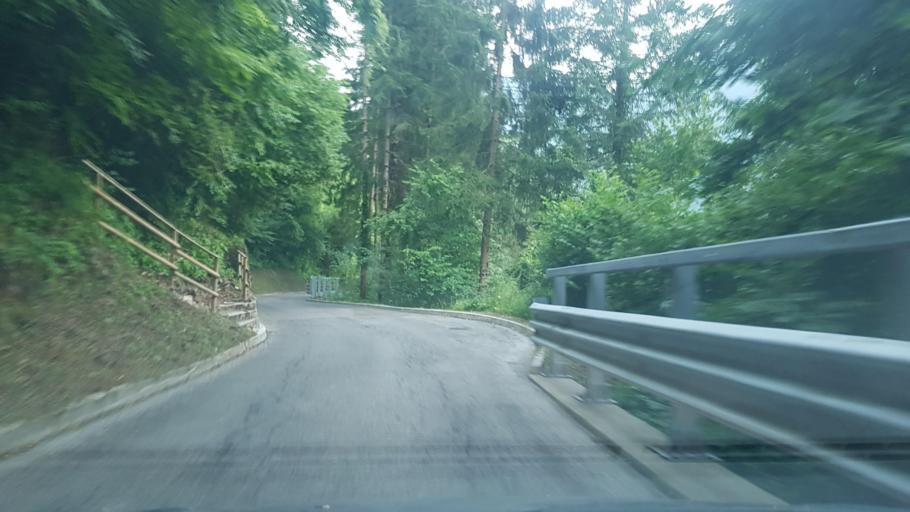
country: IT
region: Friuli Venezia Giulia
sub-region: Provincia di Udine
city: Paularo
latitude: 46.5388
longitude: 13.1214
